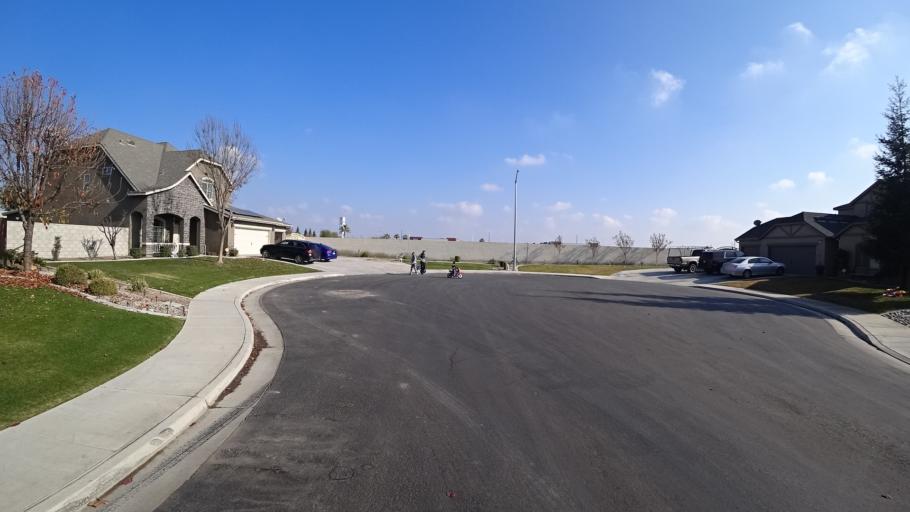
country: US
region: California
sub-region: Kern County
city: Greenacres
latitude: 35.3028
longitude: -119.1018
